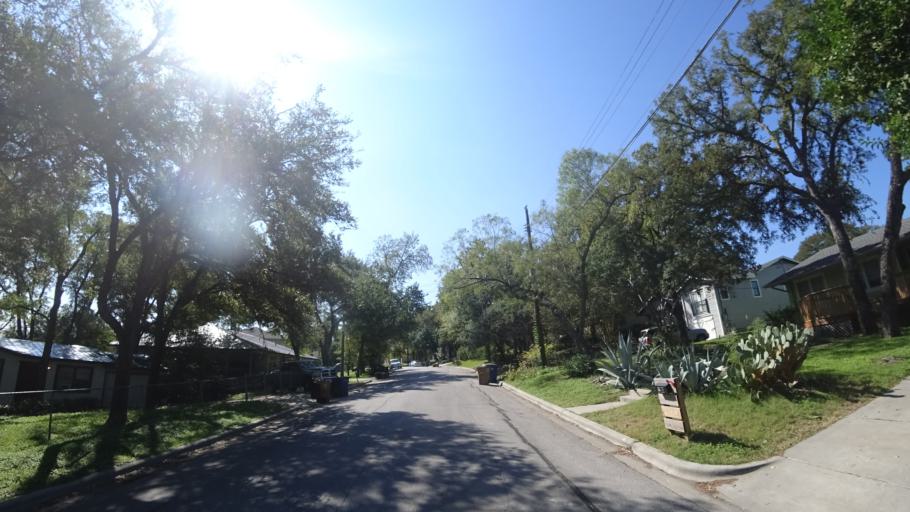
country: US
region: Texas
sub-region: Travis County
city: Austin
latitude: 30.3111
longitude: -97.6753
